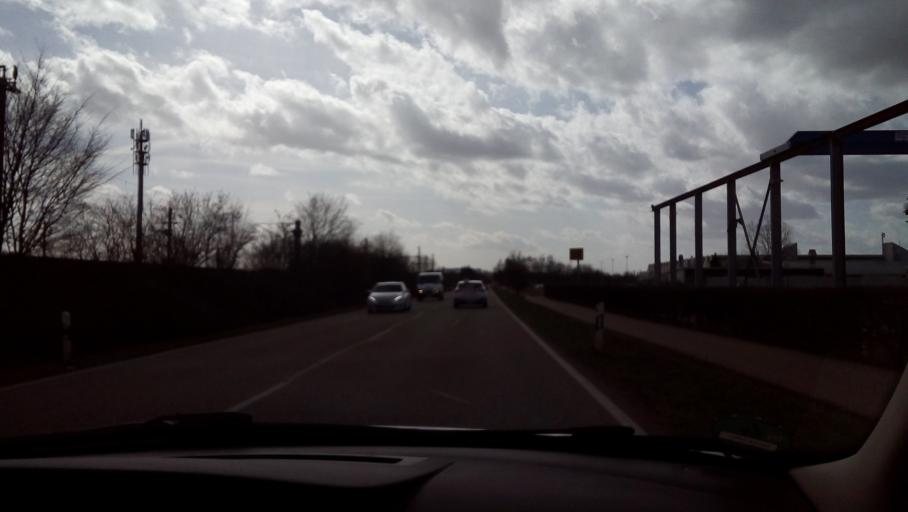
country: DE
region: Baden-Wuerttemberg
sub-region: Freiburg Region
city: Sasbach
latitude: 48.6469
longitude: 8.0804
